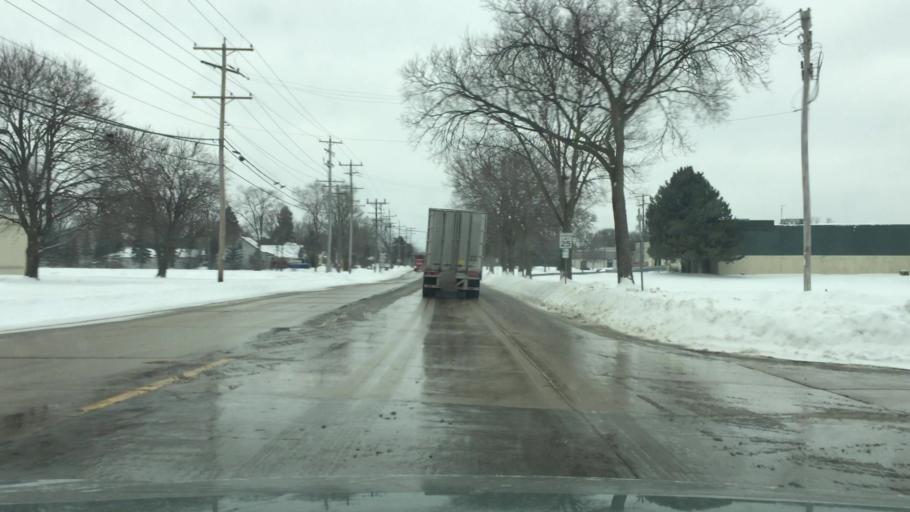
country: US
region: Wisconsin
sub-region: Waukesha County
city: Waukesha
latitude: 42.9913
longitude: -88.2434
